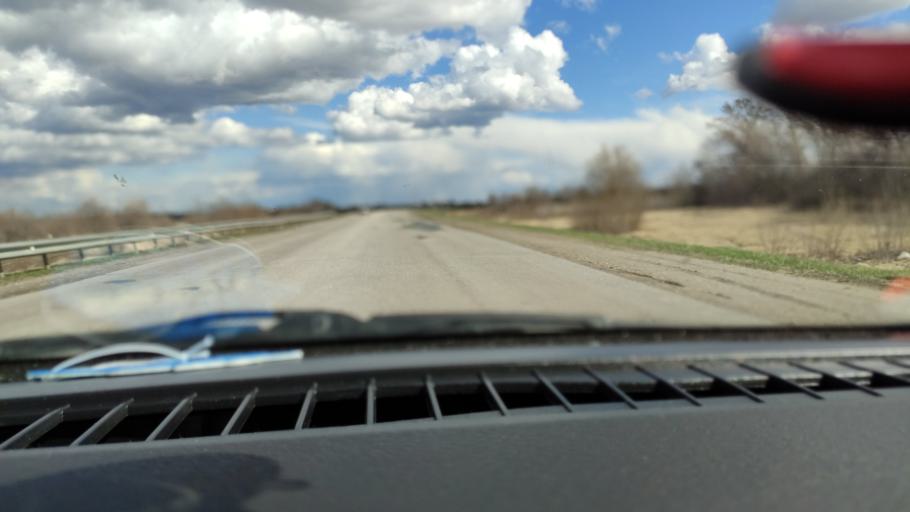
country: RU
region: Samara
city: Varlamovo
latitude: 53.1208
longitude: 48.3261
